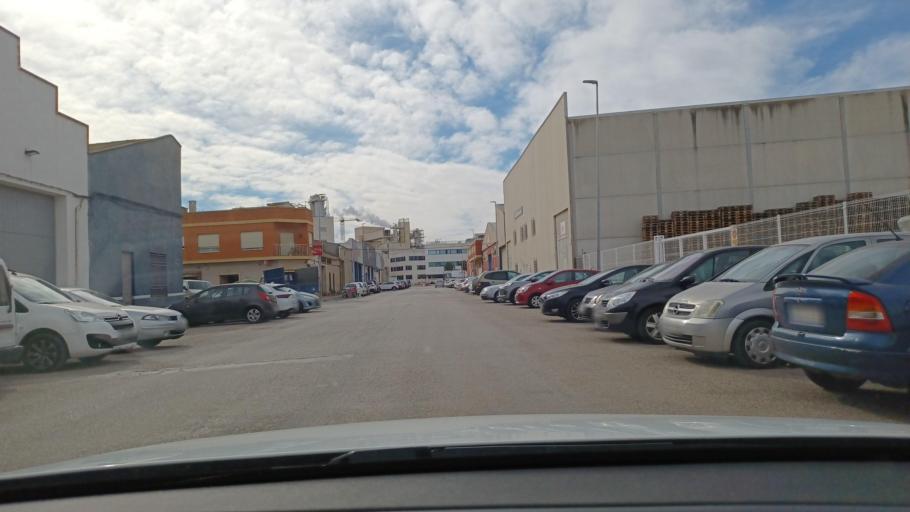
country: ES
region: Valencia
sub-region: Provincia de Valencia
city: Benifaio
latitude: 39.2861
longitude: -0.4321
